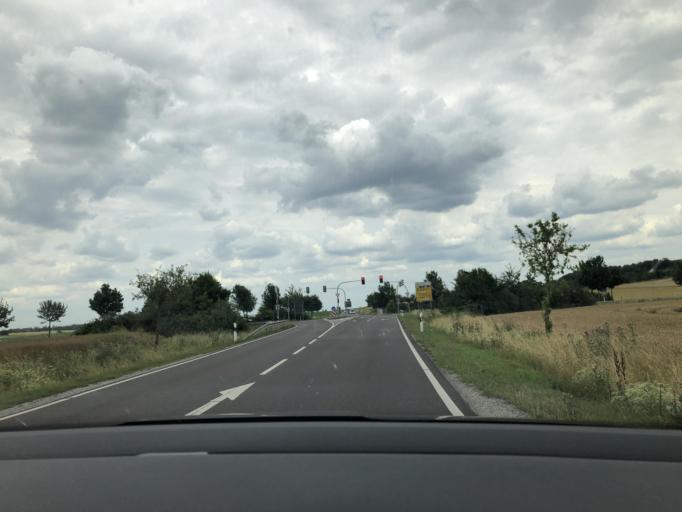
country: DE
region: Saxony-Anhalt
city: Eggersdorf
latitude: 51.9890
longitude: 11.6859
